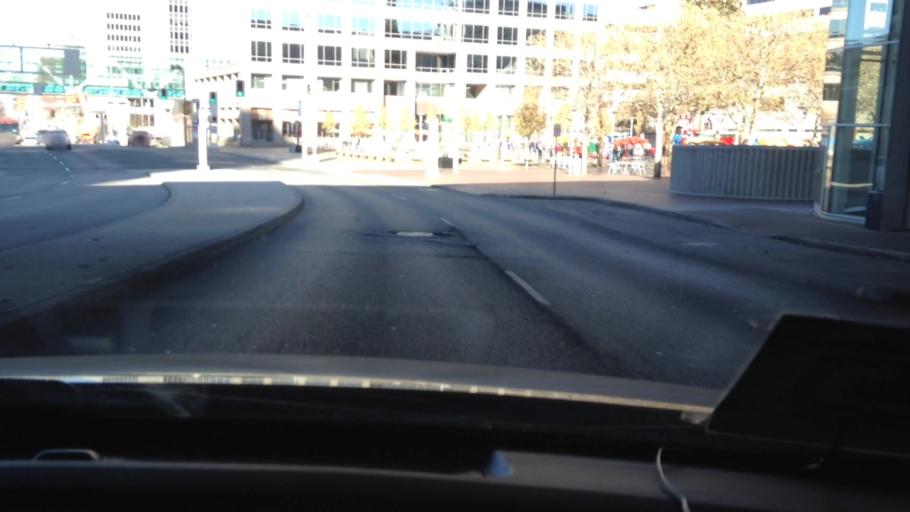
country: US
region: Missouri
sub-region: Jackson County
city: Kansas City
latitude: 39.0822
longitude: -94.5819
